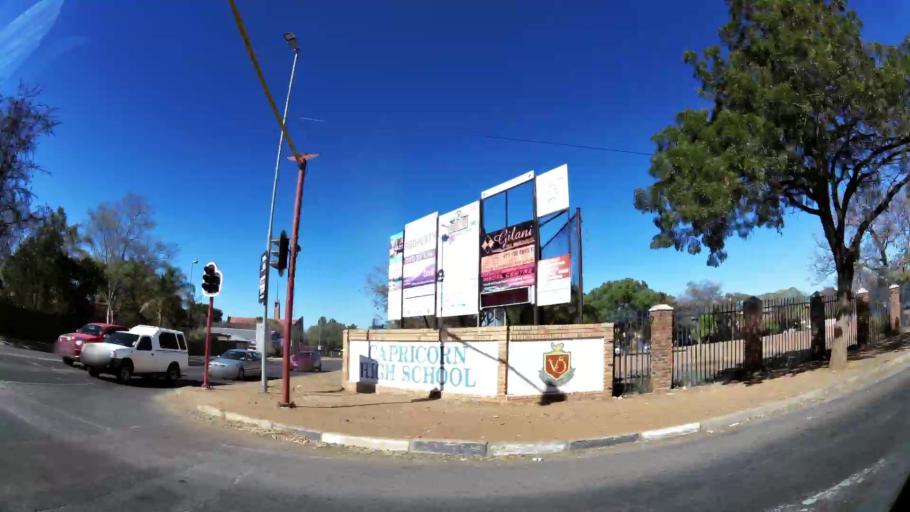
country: ZA
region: Limpopo
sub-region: Capricorn District Municipality
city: Polokwane
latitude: -23.9074
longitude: 29.4734
